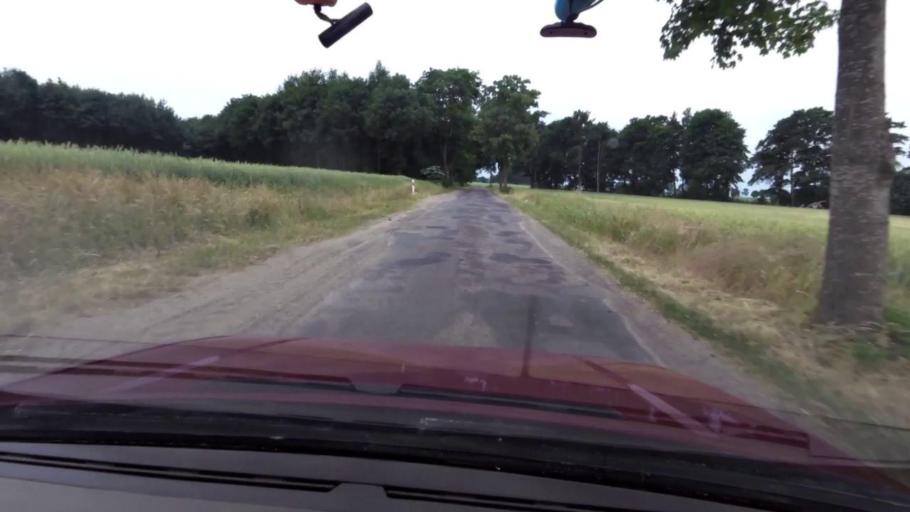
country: PL
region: Pomeranian Voivodeship
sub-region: Powiat slupski
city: Kepice
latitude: 54.2062
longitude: 16.8196
